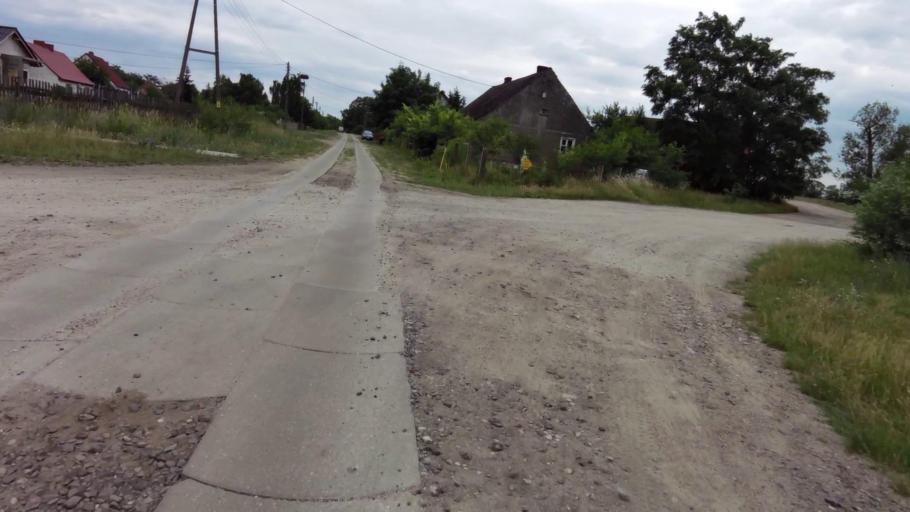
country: PL
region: Lubusz
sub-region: Powiat gorzowski
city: Kostrzyn nad Odra
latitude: 52.6211
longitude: 14.5869
